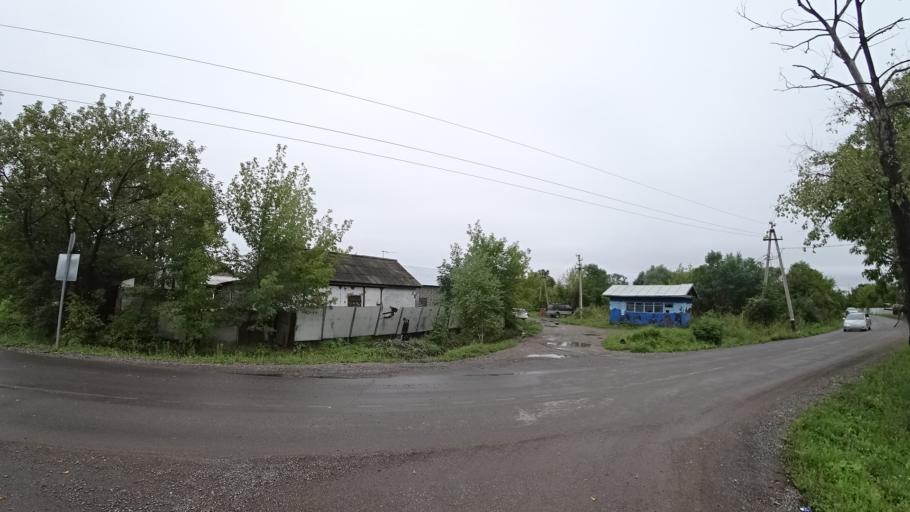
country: RU
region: Primorskiy
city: Monastyrishche
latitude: 44.2084
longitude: 132.4368
